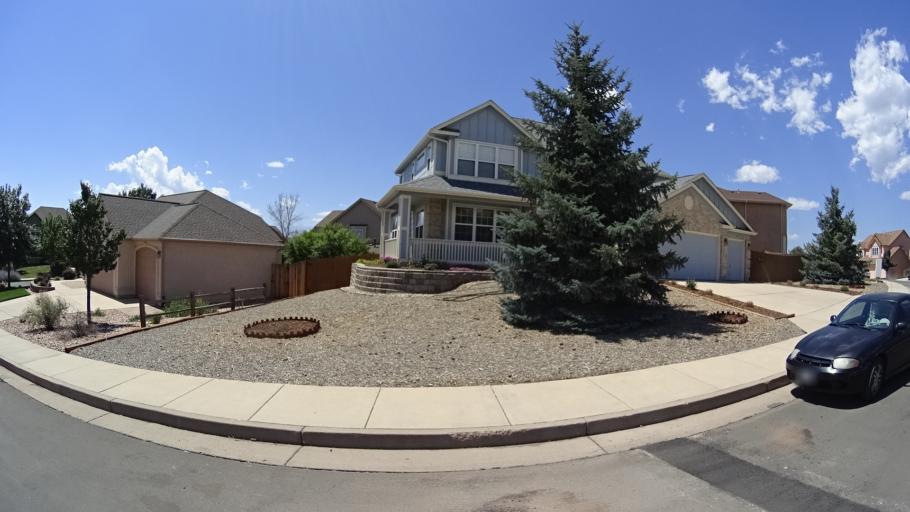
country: US
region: Colorado
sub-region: El Paso County
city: Black Forest
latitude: 38.9558
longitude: -104.7594
